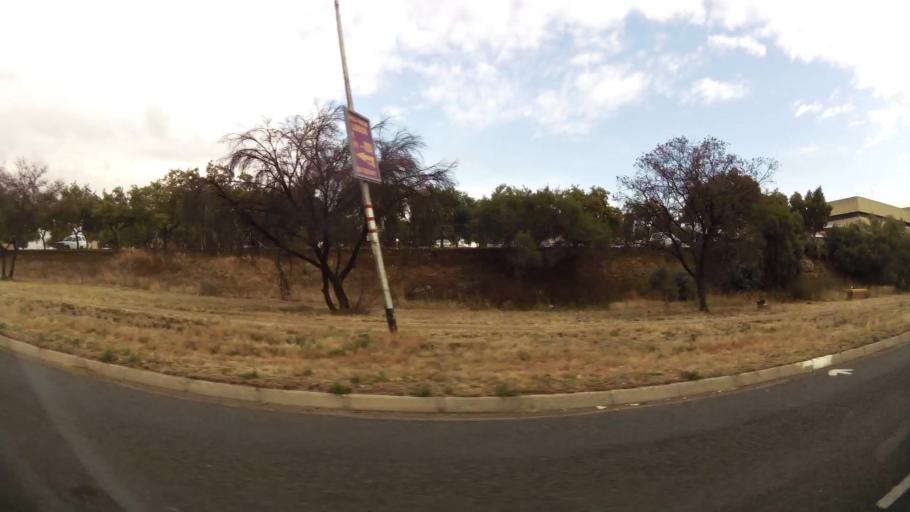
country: ZA
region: Orange Free State
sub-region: Mangaung Metropolitan Municipality
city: Bloemfontein
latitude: -29.1114
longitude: 26.1835
